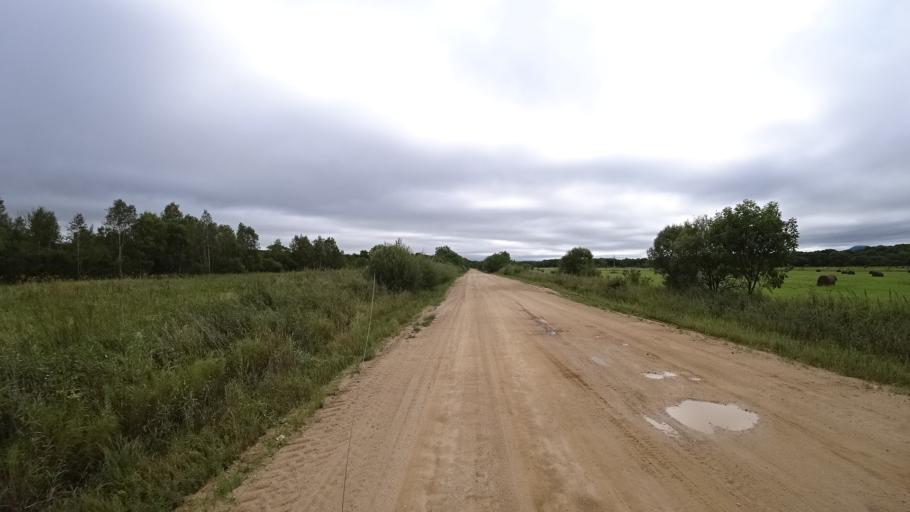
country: RU
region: Primorskiy
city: Monastyrishche
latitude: 44.1044
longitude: 132.6105
